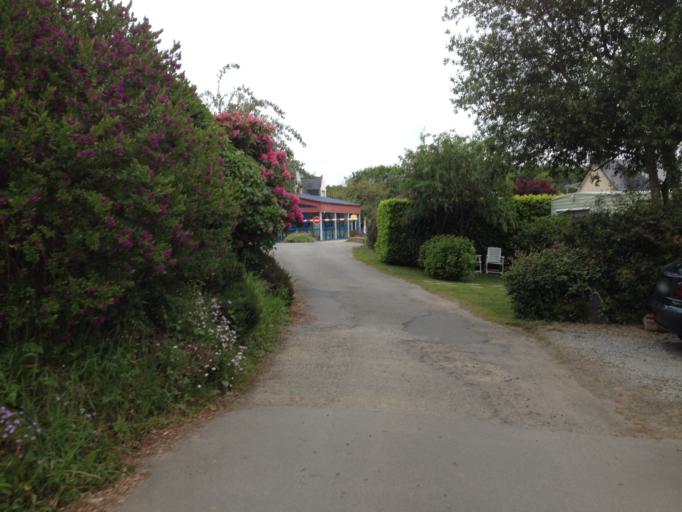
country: FR
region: Brittany
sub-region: Departement du Finistere
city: Roscanvel
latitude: 48.3651
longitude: -4.5395
